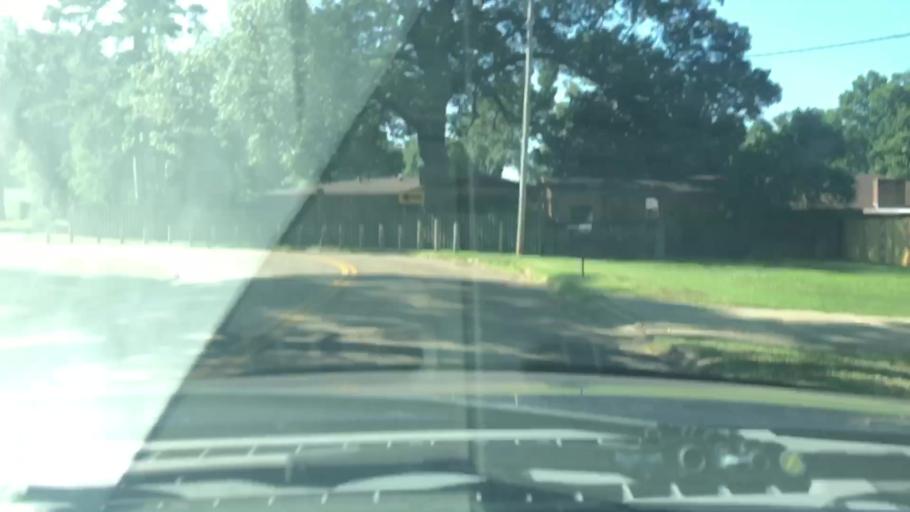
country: US
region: Arkansas
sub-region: Miller County
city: Texarkana
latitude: 33.4592
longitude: -94.0583
